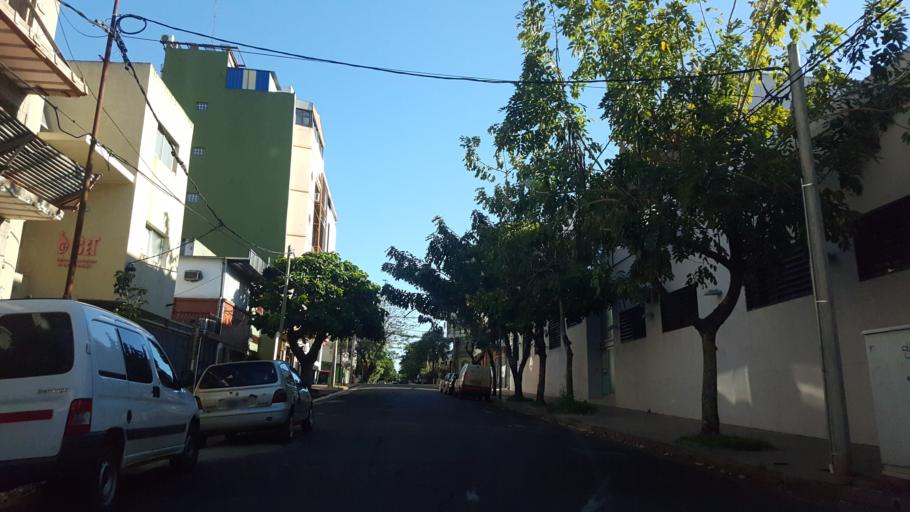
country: AR
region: Misiones
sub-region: Departamento de Capital
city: Posadas
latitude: -27.3654
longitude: -55.8998
